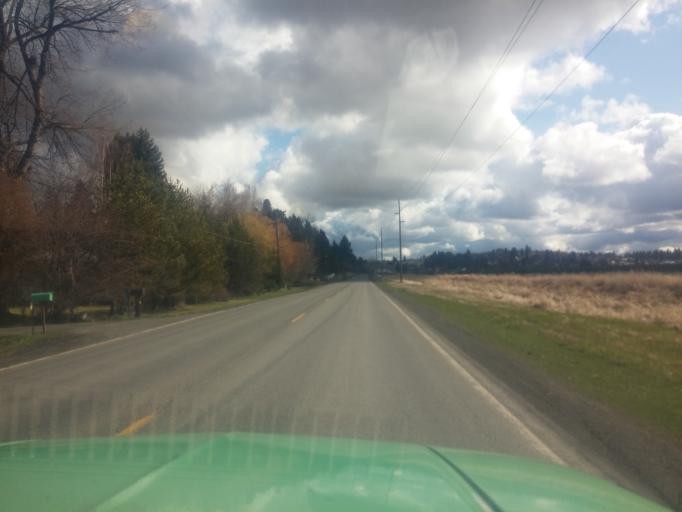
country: US
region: Idaho
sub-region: Latah County
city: Moscow
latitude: 46.9301
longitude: -116.9172
